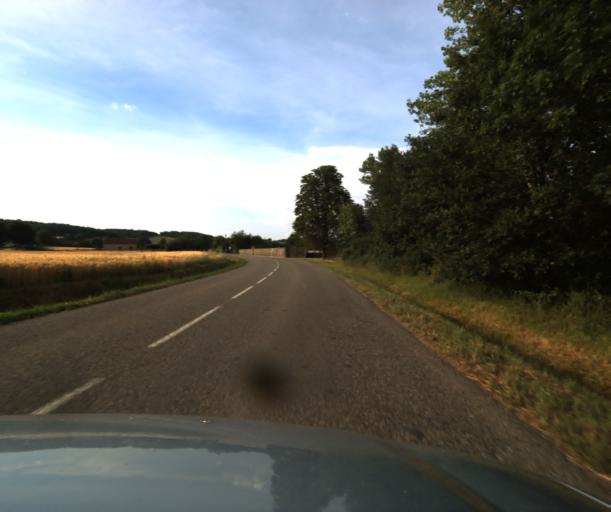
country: FR
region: Midi-Pyrenees
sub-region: Departement du Tarn-et-Garonne
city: Castelsarrasin
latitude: 43.9520
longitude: 1.1028
